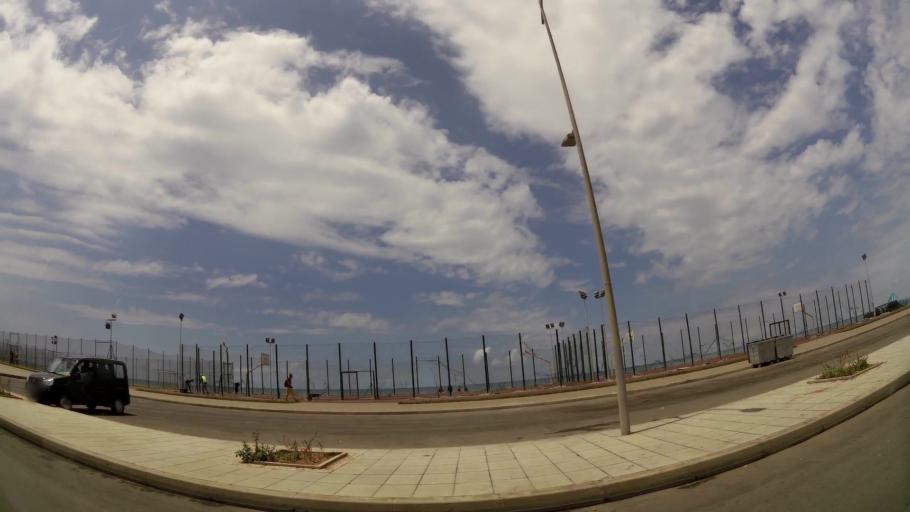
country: MA
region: Rabat-Sale-Zemmour-Zaer
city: Sale
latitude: 34.0577
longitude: -6.8190
